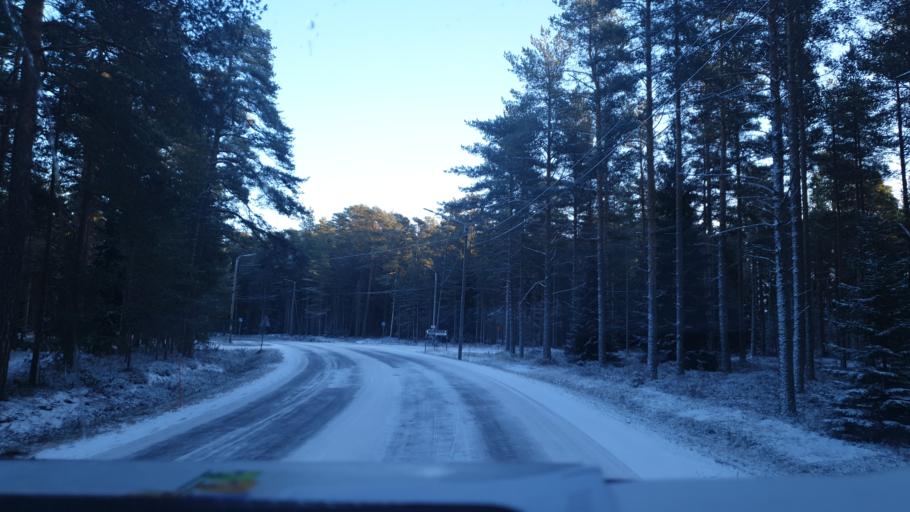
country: FI
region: Central Ostrobothnia
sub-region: Kokkola
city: Kokkola
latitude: 63.8194
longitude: 23.0719
